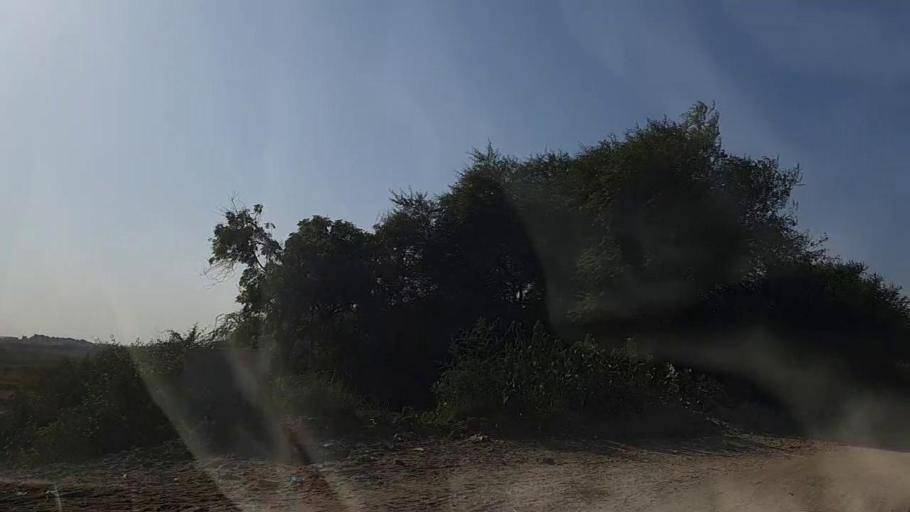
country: PK
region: Sindh
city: Mirpur Batoro
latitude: 24.5534
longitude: 68.1723
